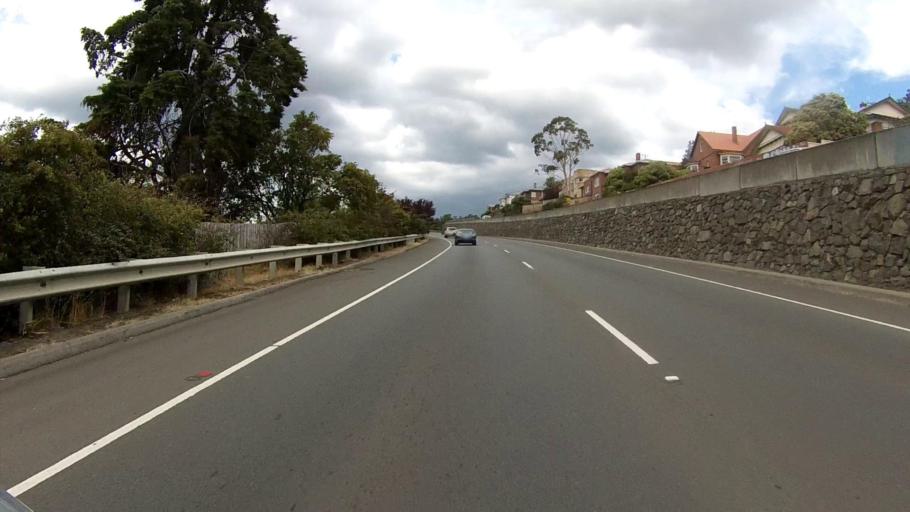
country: AU
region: Tasmania
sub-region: Hobart
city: Dynnyrne
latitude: -42.9015
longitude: 147.3161
